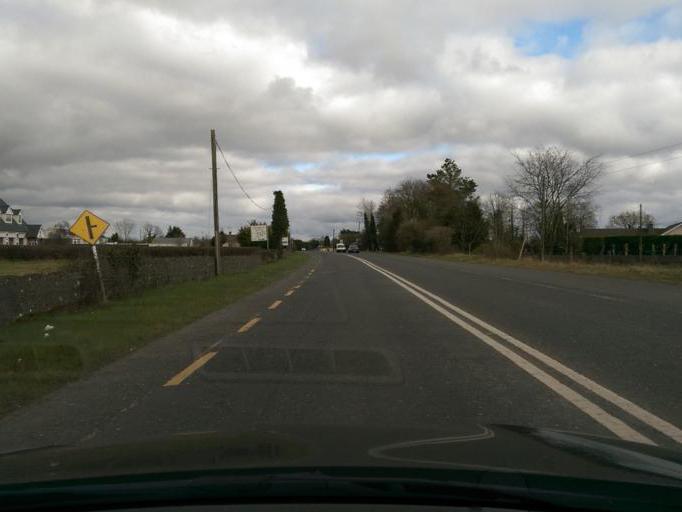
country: IE
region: Connaught
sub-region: County Galway
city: Ballinasloe
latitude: 53.3278
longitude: -8.1689
